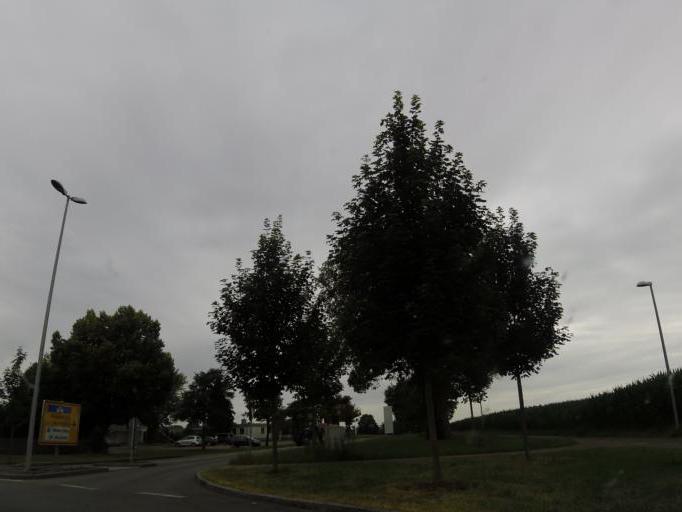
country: DE
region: Bavaria
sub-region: Upper Bavaria
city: Erding
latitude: 48.2942
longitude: 11.8914
